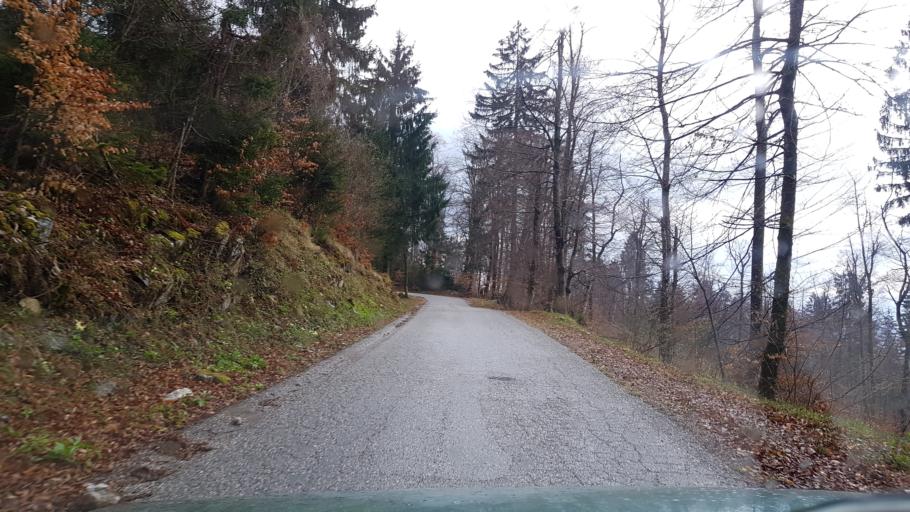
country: SI
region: Cerkno
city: Cerkno
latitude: 46.1299
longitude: 13.8673
